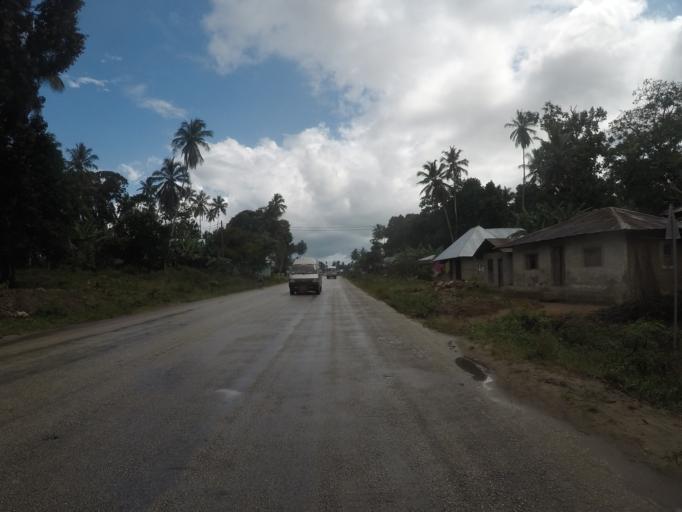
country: TZ
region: Zanzibar Central/South
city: Koani
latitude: -6.0226
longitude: 39.2409
